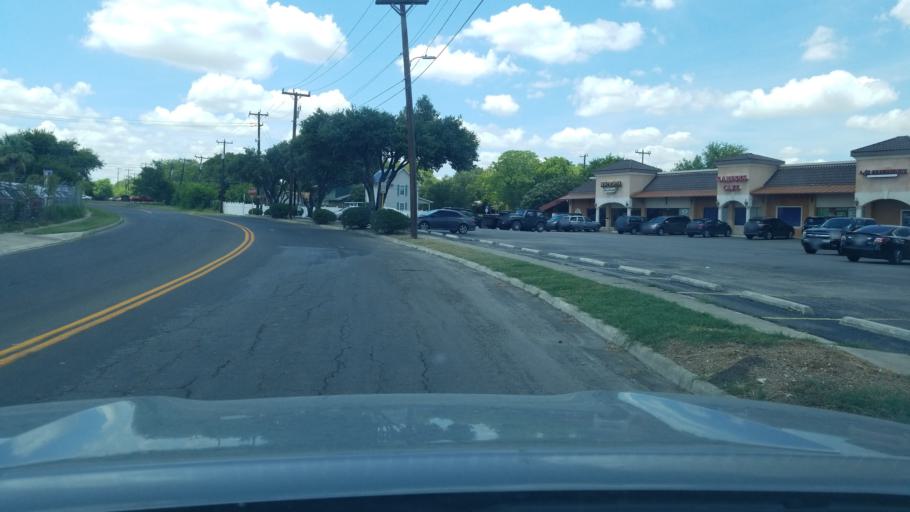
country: US
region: Texas
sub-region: Bexar County
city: Castle Hills
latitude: 29.5289
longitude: -98.4996
